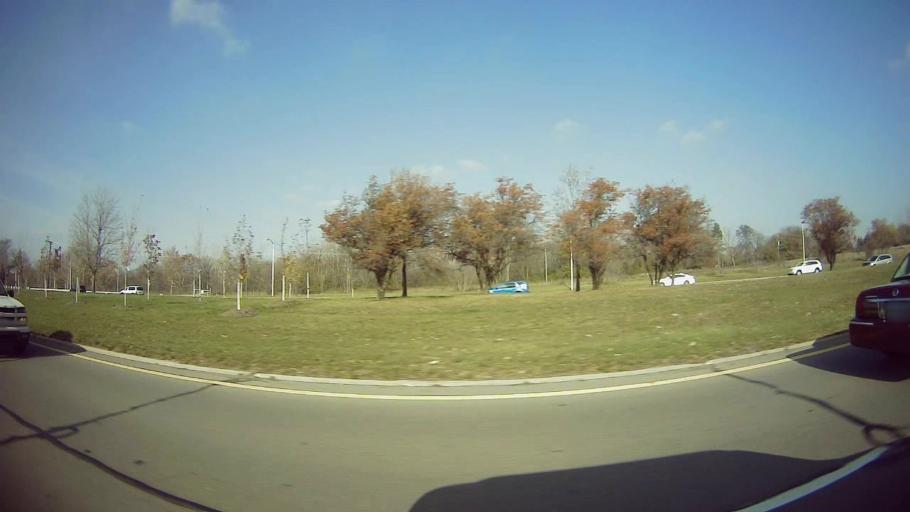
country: US
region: Michigan
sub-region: Wayne County
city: Dearborn Heights
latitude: 42.3283
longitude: -83.2386
